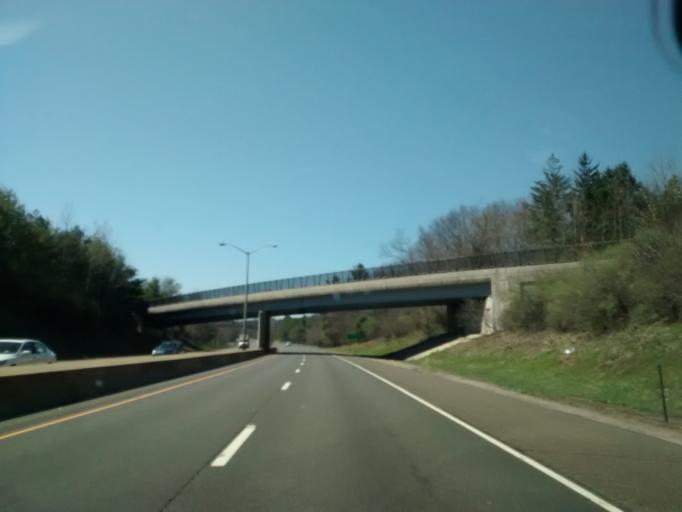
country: US
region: Connecticut
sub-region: Hartford County
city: East Hartford
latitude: 41.8002
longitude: -72.5818
